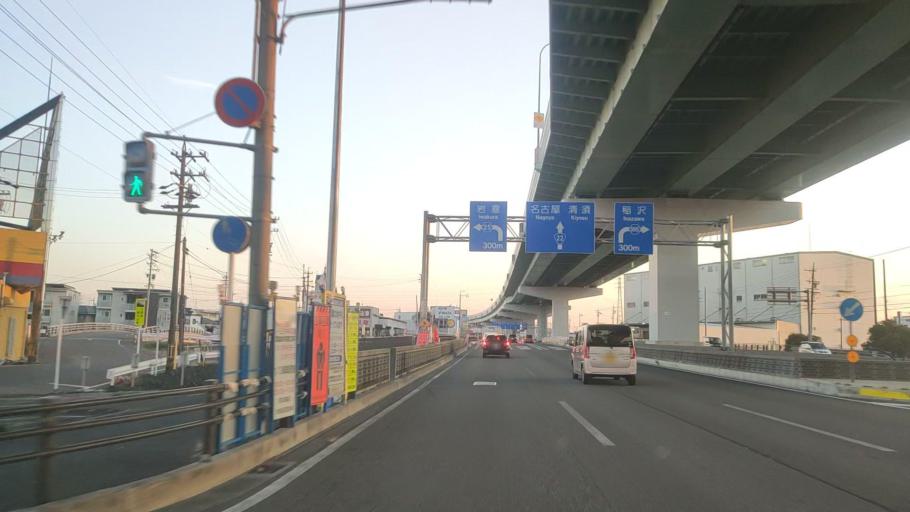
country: JP
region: Aichi
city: Iwakura
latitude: 35.2784
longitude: 136.8302
